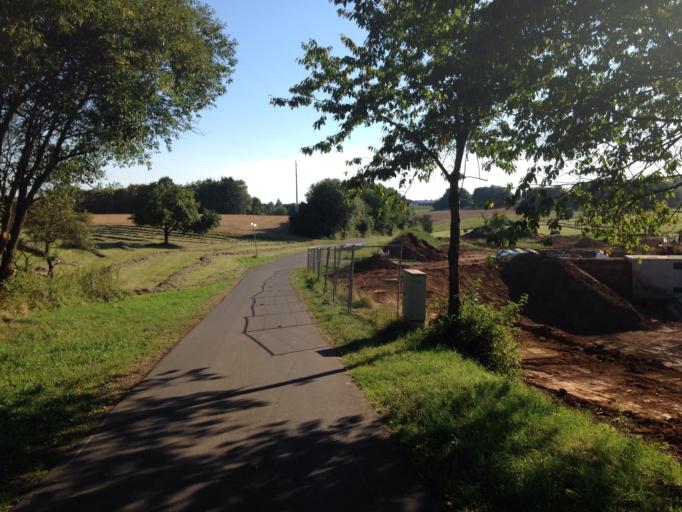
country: DE
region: Hesse
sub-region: Regierungsbezirk Giessen
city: Grunberg
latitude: 50.6016
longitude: 8.9649
